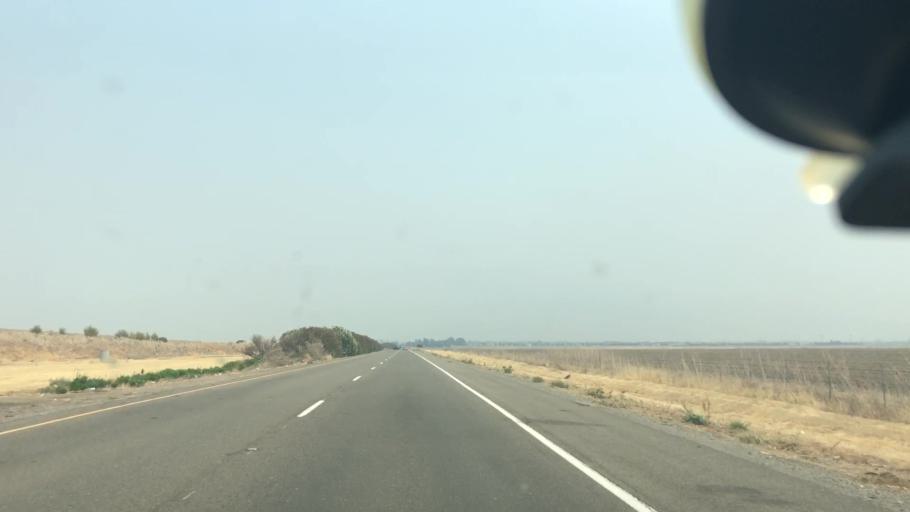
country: US
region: California
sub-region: San Joaquin County
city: Mountain House
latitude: 37.7400
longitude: -121.4945
